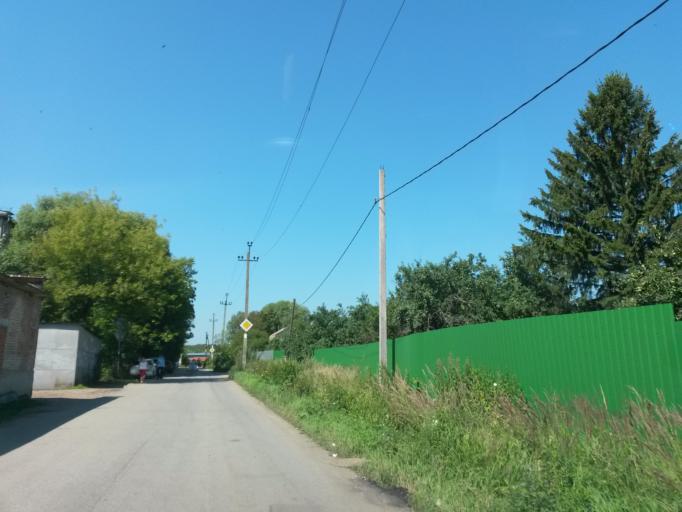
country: RU
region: Moskovskaya
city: Stolbovaya
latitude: 55.2564
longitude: 37.4863
